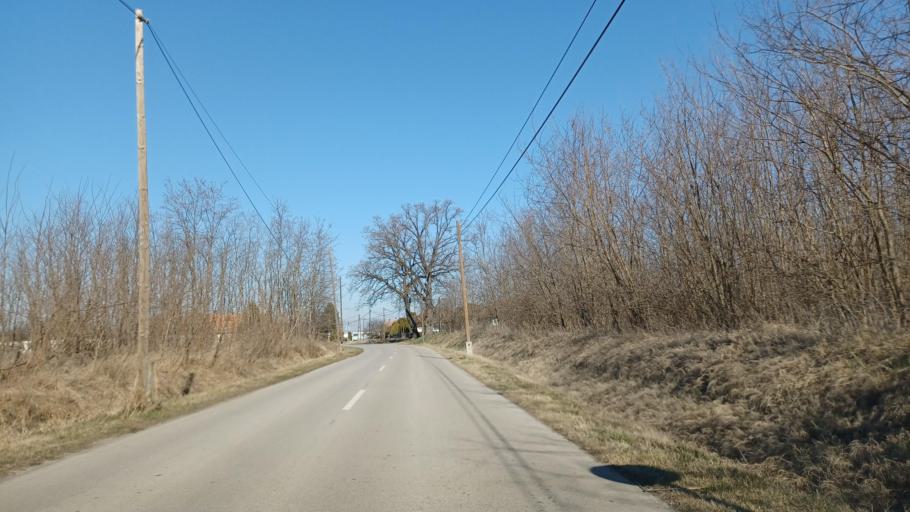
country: HU
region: Tolna
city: Tengelic
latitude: 46.5431
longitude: 18.7020
